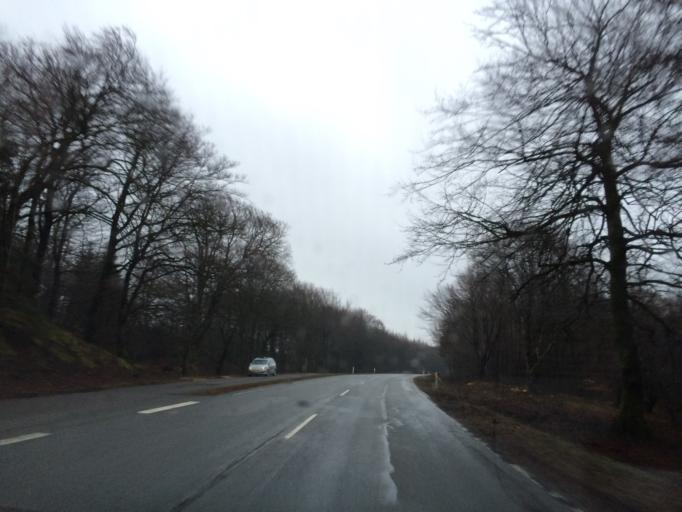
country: DK
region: North Denmark
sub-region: Mariagerfjord Kommune
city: Arden
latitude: 56.7940
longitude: 9.8211
